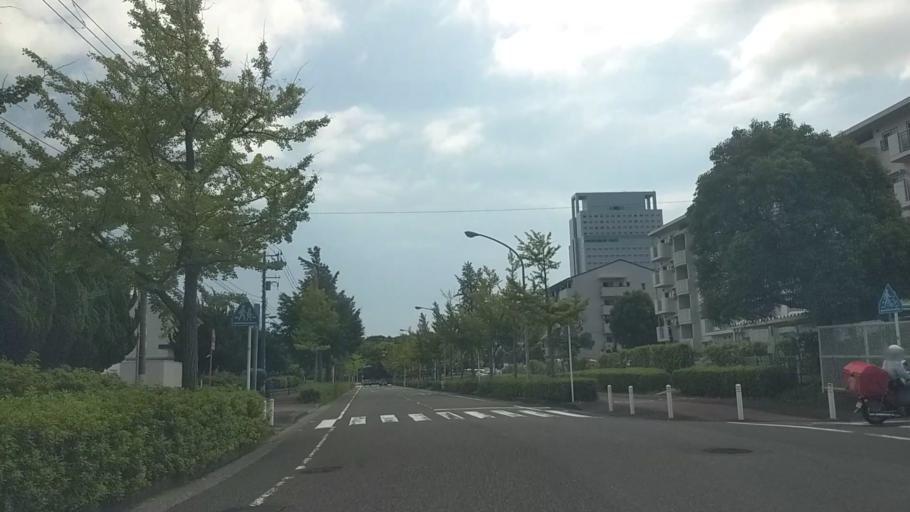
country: JP
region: Kanagawa
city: Yokosuka
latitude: 35.3552
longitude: 139.6402
